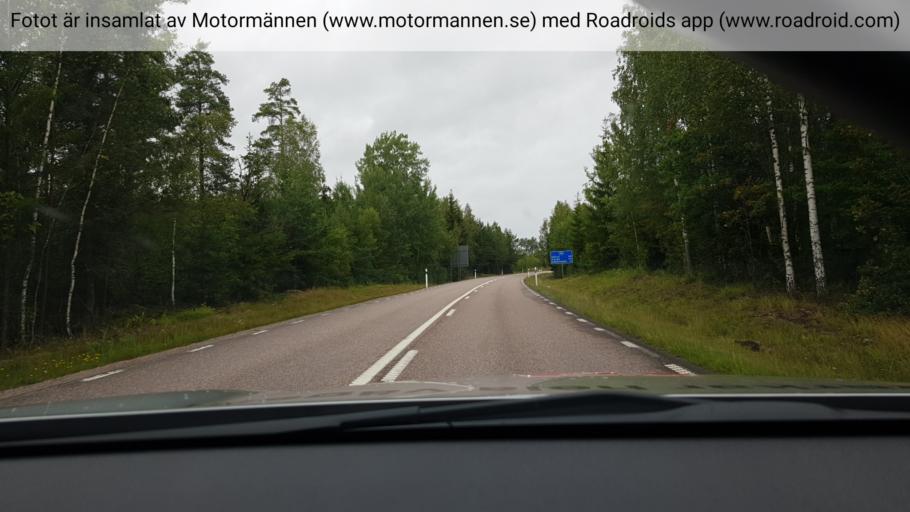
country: SE
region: Gaevleborg
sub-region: Gavle Kommun
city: Hedesunda
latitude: 60.2993
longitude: 16.9135
